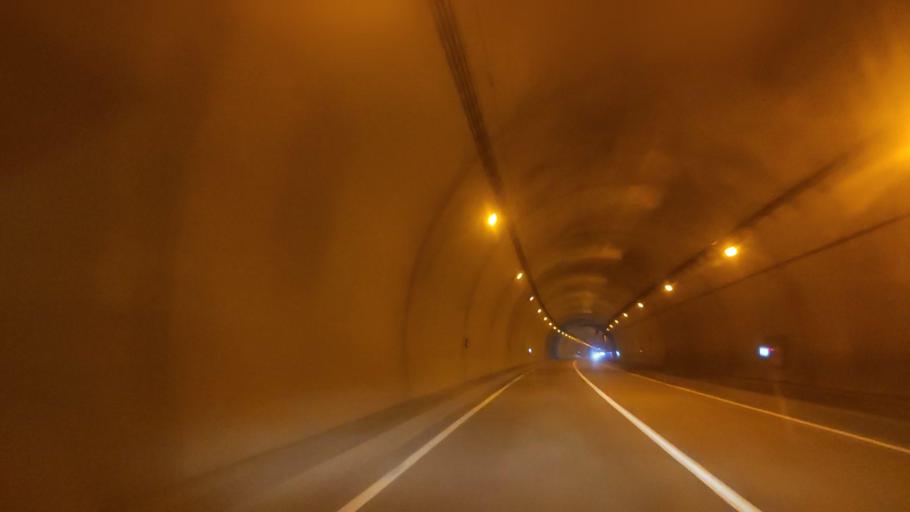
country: JP
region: Hokkaido
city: Date
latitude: 42.5625
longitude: 140.7829
